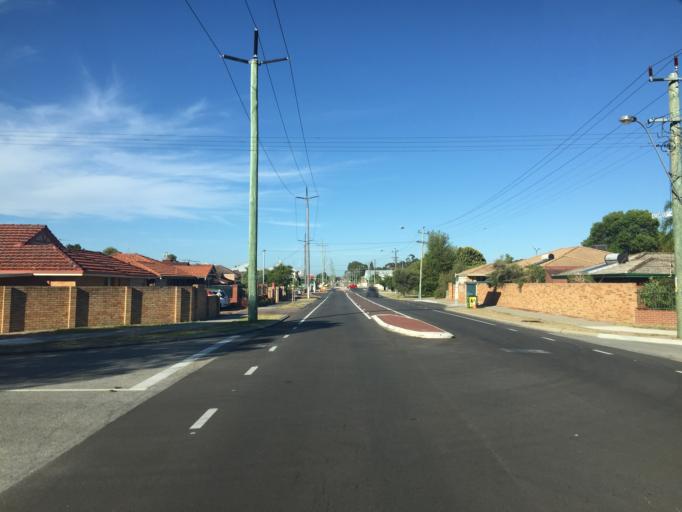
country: AU
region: Western Australia
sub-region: Belmont
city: Rivervale
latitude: -31.9627
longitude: 115.9264
